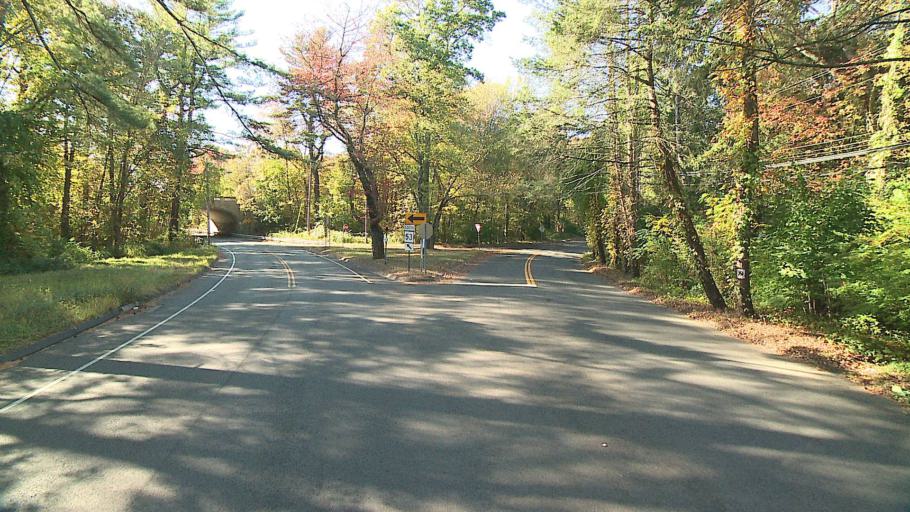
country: US
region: Connecticut
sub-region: Fairfield County
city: Westport
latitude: 41.1593
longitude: -73.3947
